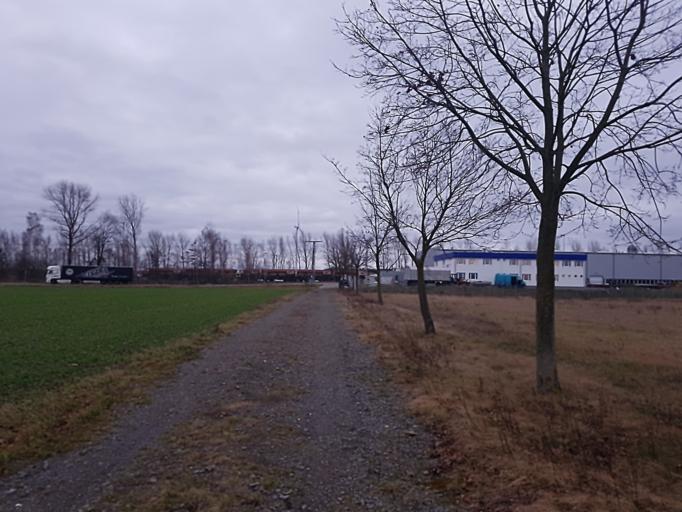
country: DE
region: Brandenburg
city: Falkenberg
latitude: 51.5868
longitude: 13.2853
